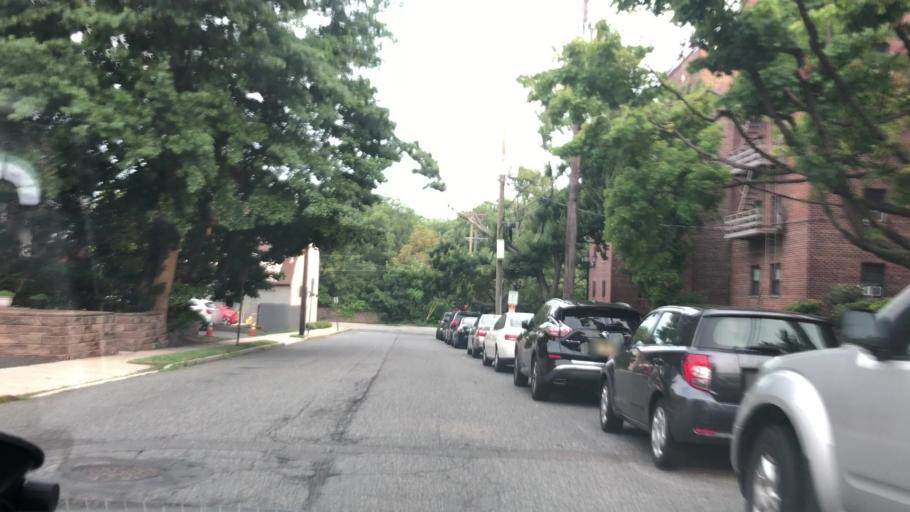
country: US
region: New Jersey
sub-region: Bergen County
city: Fort Lee
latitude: 40.8615
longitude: -73.9602
